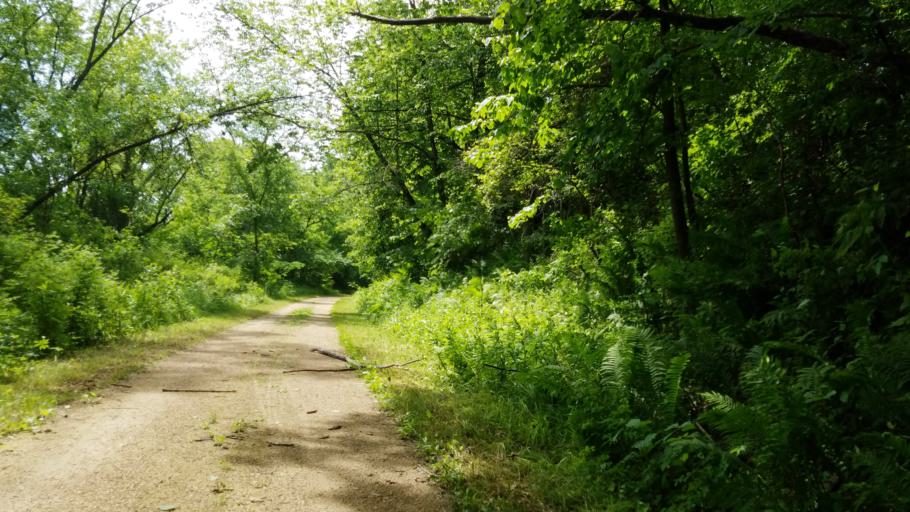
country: US
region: Wisconsin
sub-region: Dunn County
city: Menomonie
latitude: 44.8086
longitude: -91.9480
